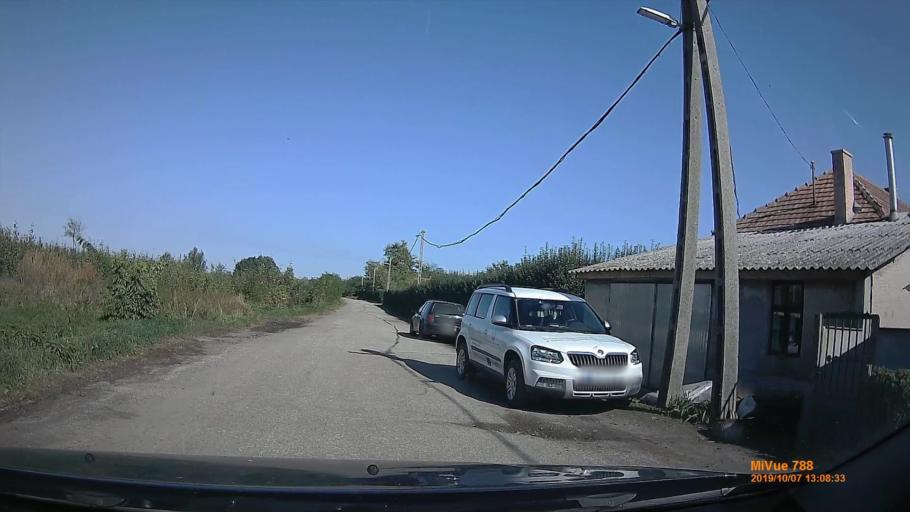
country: HU
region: Jasz-Nagykun-Szolnok
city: Cserkeszolo
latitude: 46.8738
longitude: 20.1810
